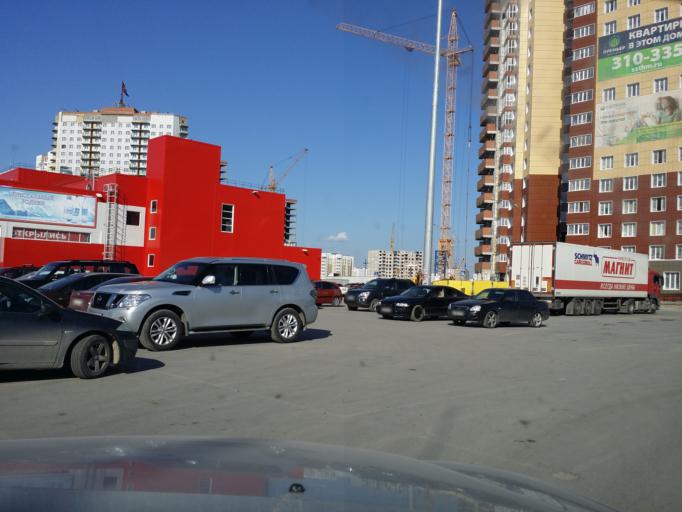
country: RU
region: Khanty-Mansiyskiy Avtonomnyy Okrug
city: Nizhnevartovsk
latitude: 60.9287
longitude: 76.6080
